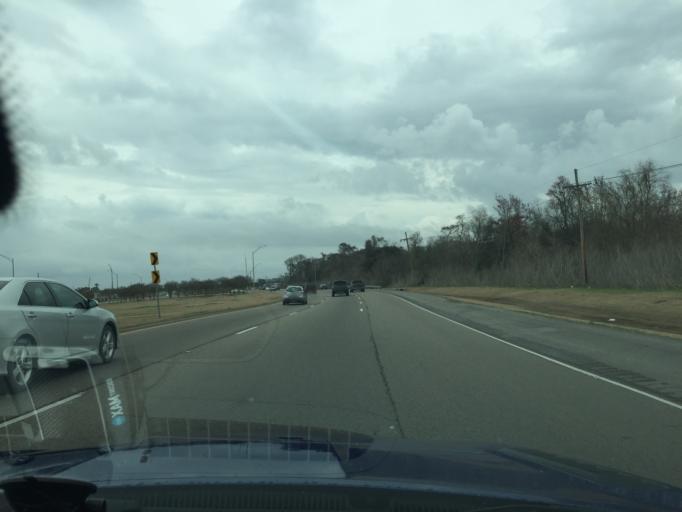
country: US
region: Louisiana
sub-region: Jefferson Parish
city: Westwego
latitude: 29.9055
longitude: -90.1582
